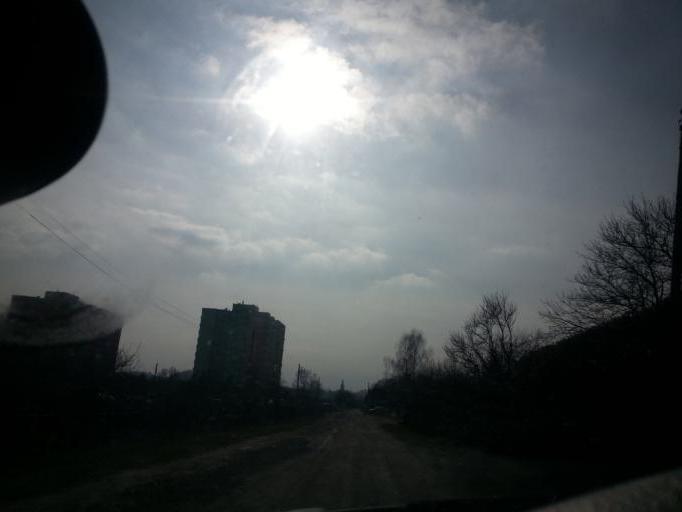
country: PL
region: Lower Silesian Voivodeship
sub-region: Powiat jeleniogorski
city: Jezow Sudecki
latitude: 50.9161
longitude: 15.7427
